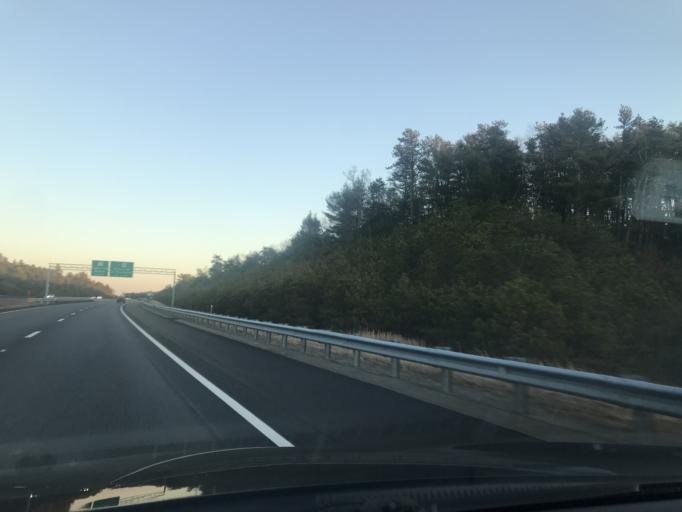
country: US
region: Massachusetts
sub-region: Plymouth County
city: Kingston
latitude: 41.9609
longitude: -70.7350
